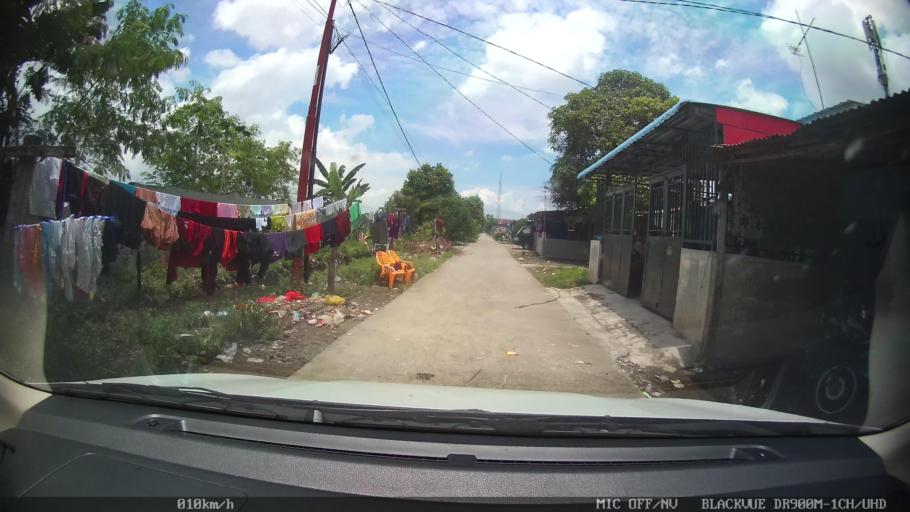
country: ID
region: North Sumatra
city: Medan
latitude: 3.6107
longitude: 98.7216
